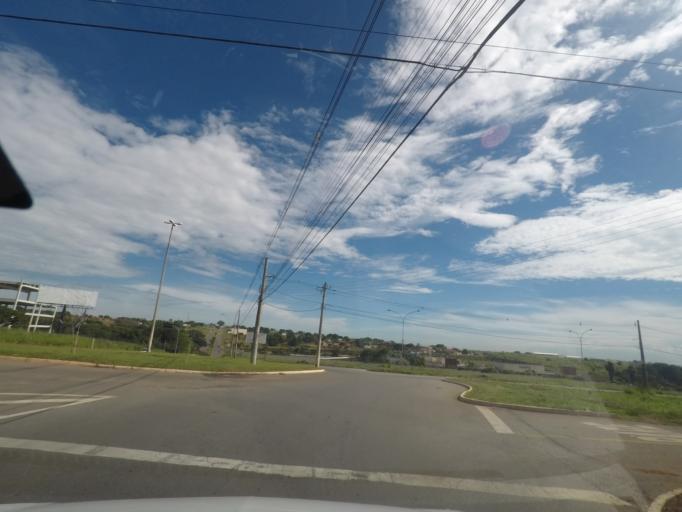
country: BR
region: Goias
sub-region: Aparecida De Goiania
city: Aparecida de Goiania
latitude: -16.8181
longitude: -49.2791
